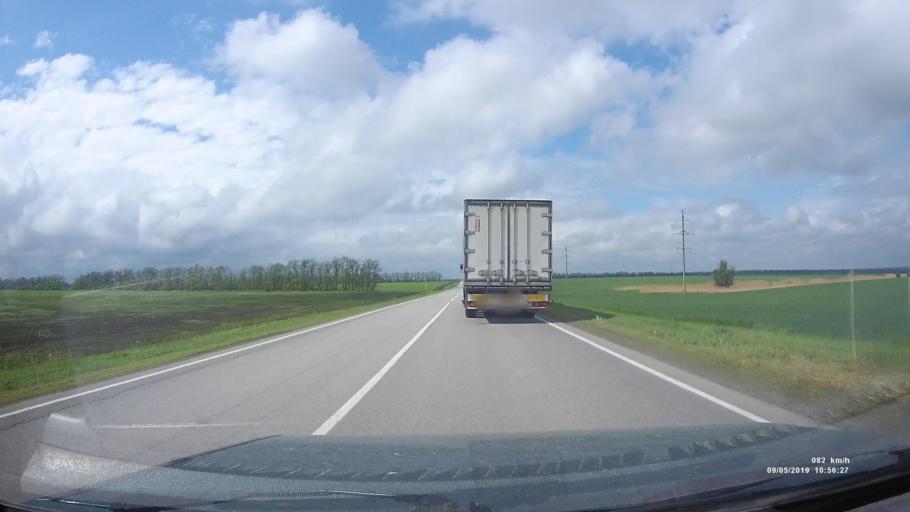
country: RU
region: Rostov
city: Peshkovo
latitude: 46.8692
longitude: 39.2983
